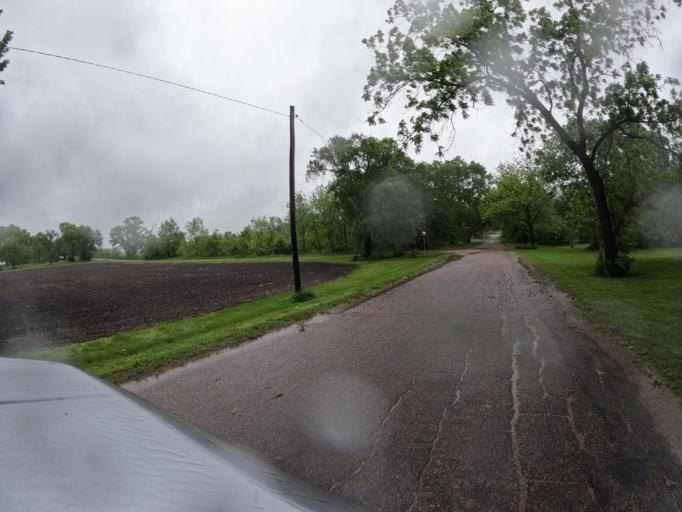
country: US
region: Nebraska
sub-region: Gage County
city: Wymore
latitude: 40.1233
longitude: -96.6550
